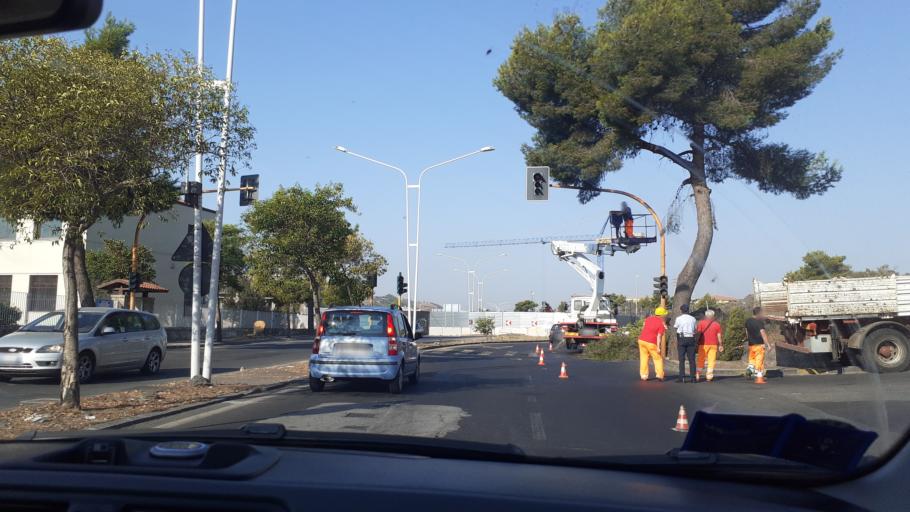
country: IT
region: Sicily
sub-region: Catania
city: Misterbianco
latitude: 37.5147
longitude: 15.0449
